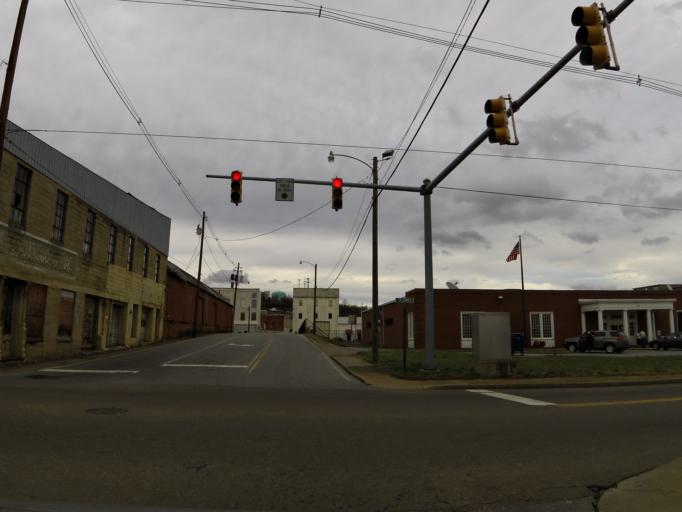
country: US
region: Tennessee
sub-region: Greene County
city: Greeneville
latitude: 36.1638
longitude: -82.8358
